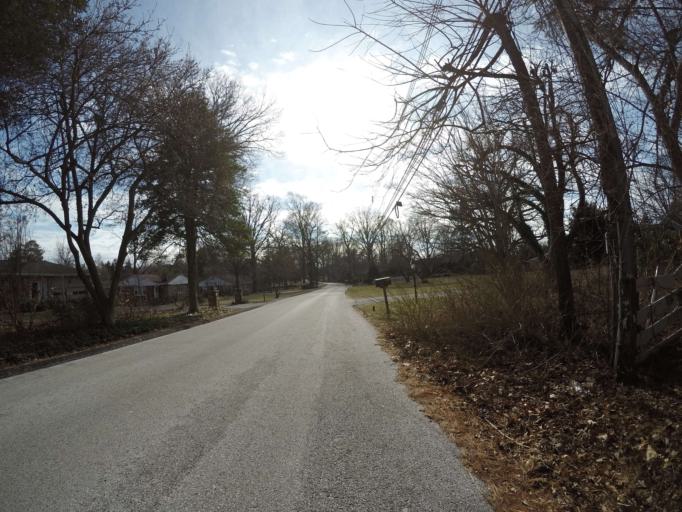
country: US
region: Maryland
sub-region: Howard County
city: Columbia
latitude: 39.2667
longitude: -76.8332
